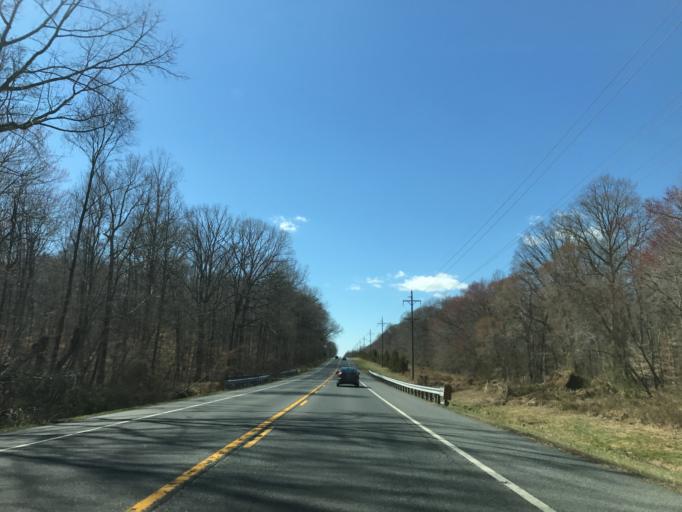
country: US
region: Maryland
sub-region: Queen Anne's County
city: Kingstown
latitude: 39.2646
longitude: -75.8805
